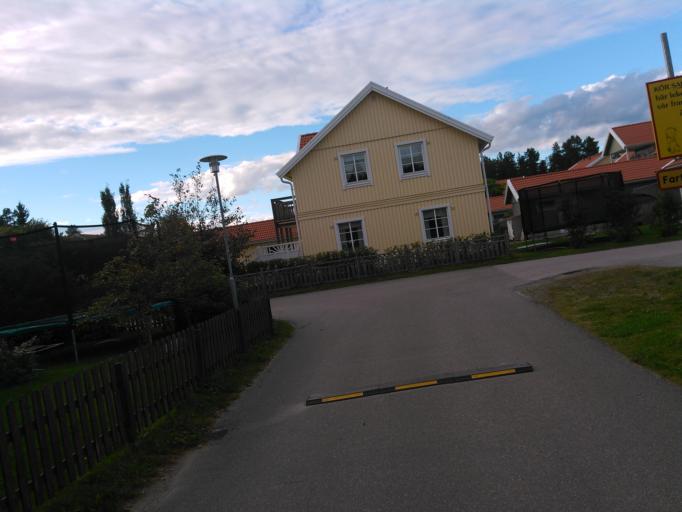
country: SE
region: Vaesterbotten
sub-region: Umea Kommun
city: Ersmark
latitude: 63.8050
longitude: 20.3392
